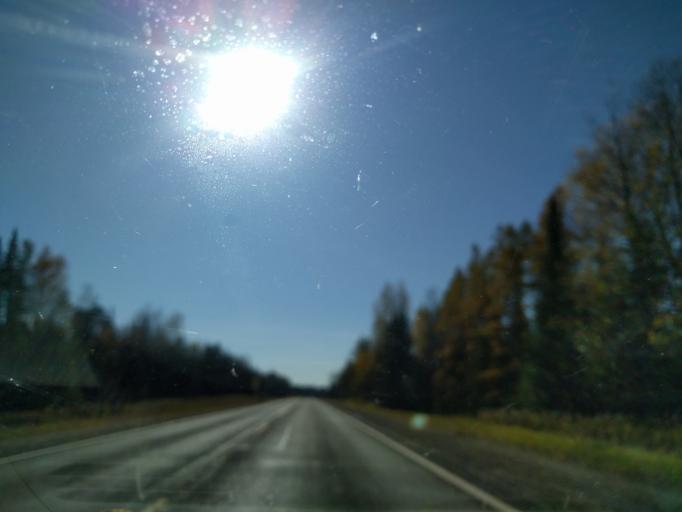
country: US
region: Michigan
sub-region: Marquette County
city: West Ishpeming
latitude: 46.2942
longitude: -88.0043
